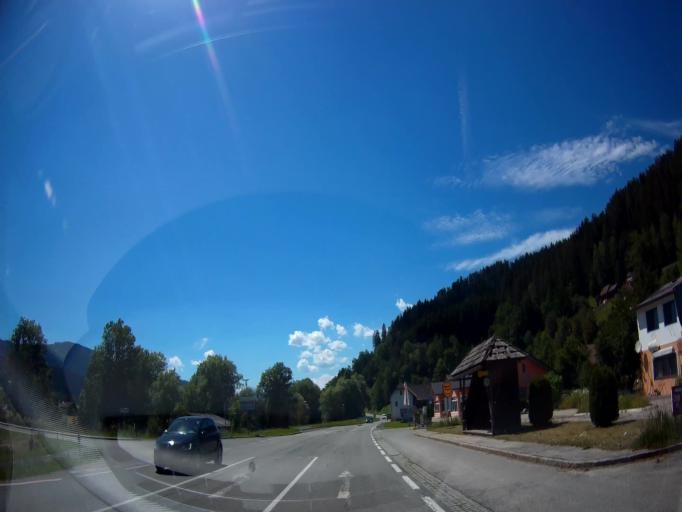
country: AT
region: Carinthia
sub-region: Politischer Bezirk Sankt Veit an der Glan
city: Glodnitz
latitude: 46.8498
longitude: 14.2004
